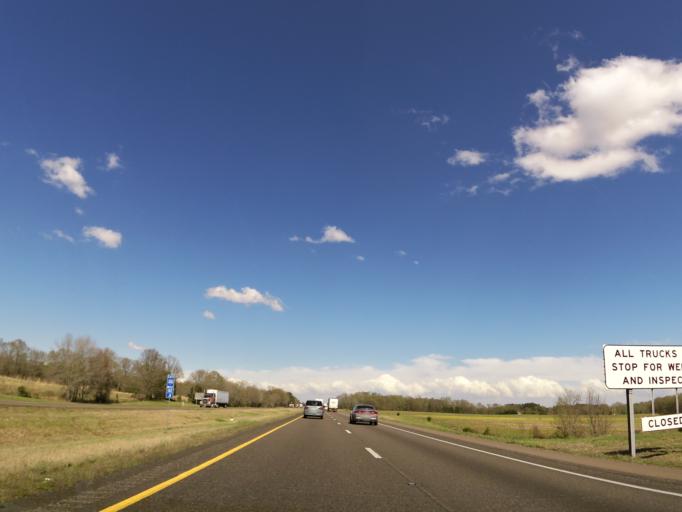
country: US
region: Tennessee
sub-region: Henderson County
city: Lexington
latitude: 35.7609
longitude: -88.4857
